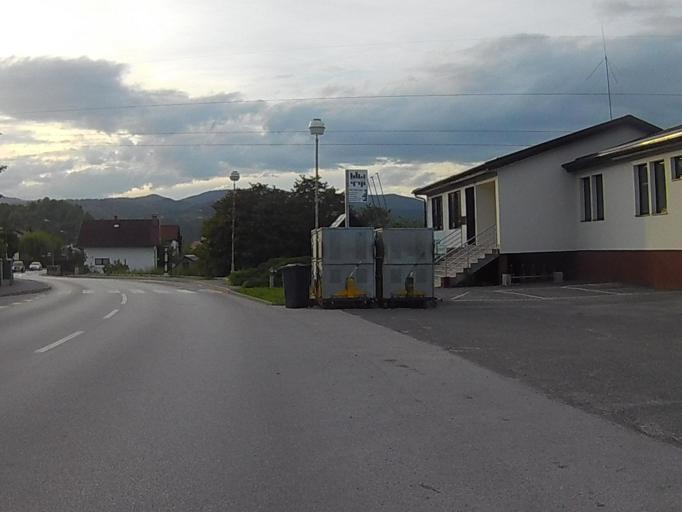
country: SI
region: Maribor
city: Limbus
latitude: 46.5502
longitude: 15.5887
